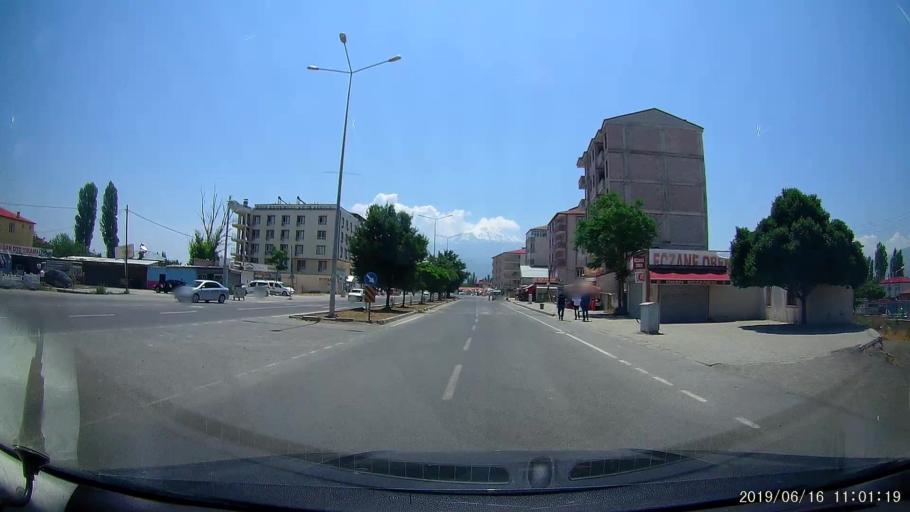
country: TR
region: Igdir
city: Igdir
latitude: 39.9157
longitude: 44.0489
